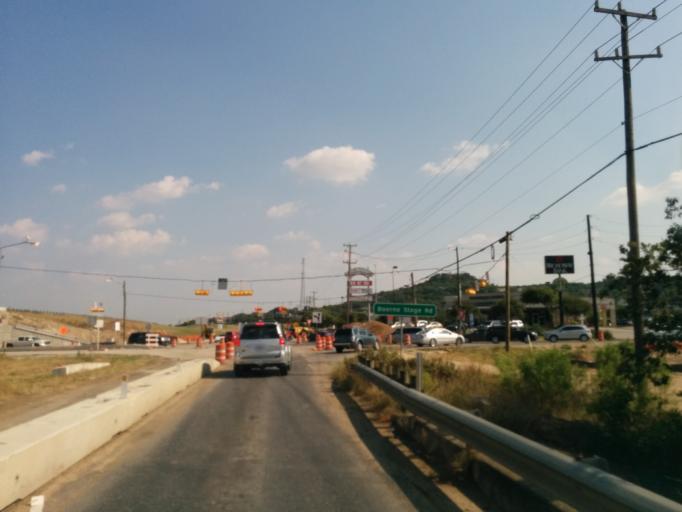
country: US
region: Texas
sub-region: Bexar County
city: Cross Mountain
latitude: 29.6671
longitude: -98.6326
